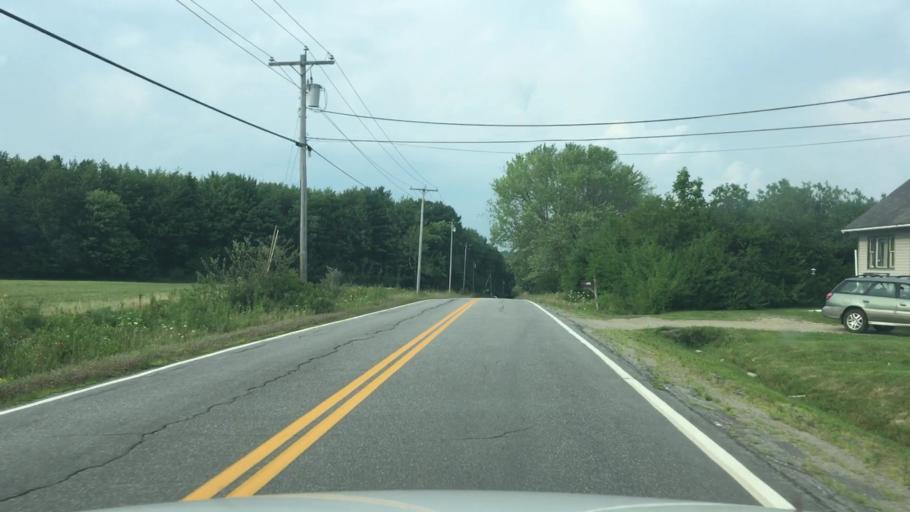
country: US
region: Maine
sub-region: Knox County
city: Washington
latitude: 44.2834
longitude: -69.3669
